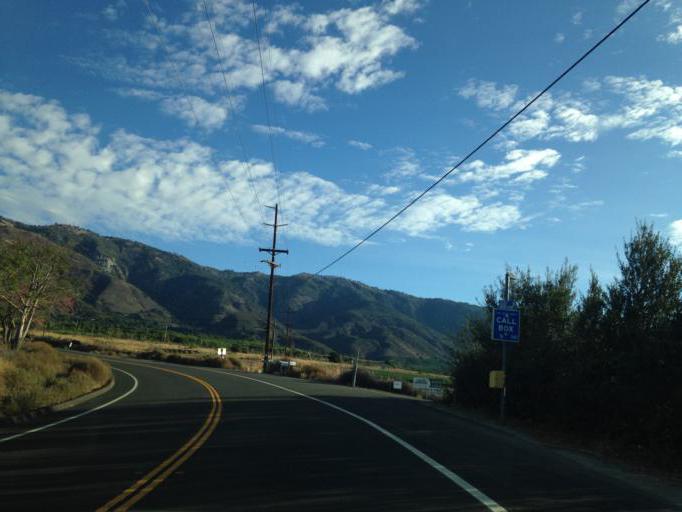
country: US
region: California
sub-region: San Diego County
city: Valley Center
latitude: 33.2960
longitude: -116.9442
